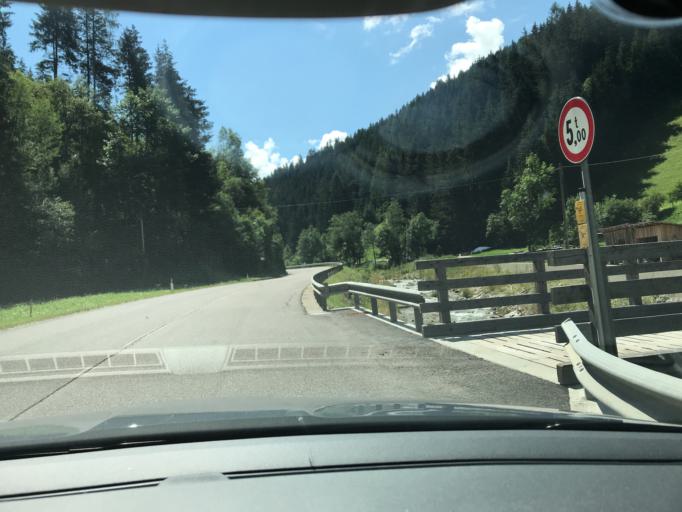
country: IT
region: Trentino-Alto Adige
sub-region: Bolzano
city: San Vigilio
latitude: 46.7167
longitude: 11.9042
